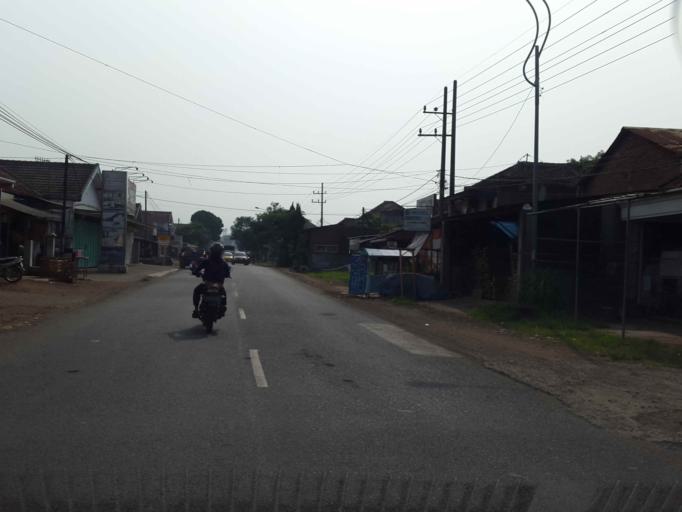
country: ID
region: East Java
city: Tamiajeng
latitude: -7.9542
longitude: 112.7030
